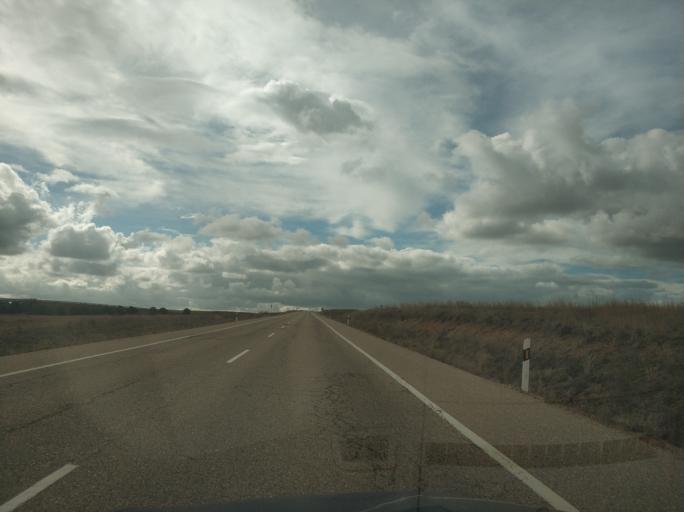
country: ES
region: Castille and Leon
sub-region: Provincia de Valladolid
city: Pollos
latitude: 41.4394
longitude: -5.0962
